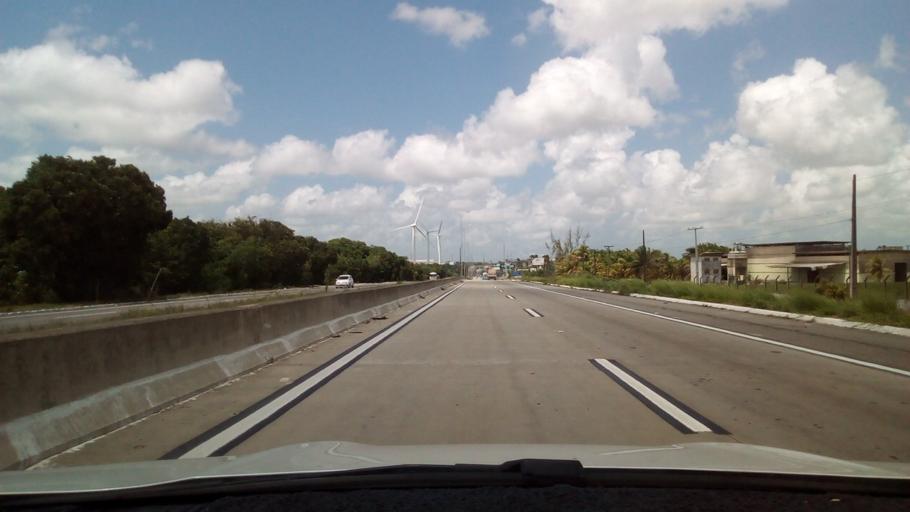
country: BR
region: Paraiba
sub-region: Conde
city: Conde
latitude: -7.2791
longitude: -34.9389
